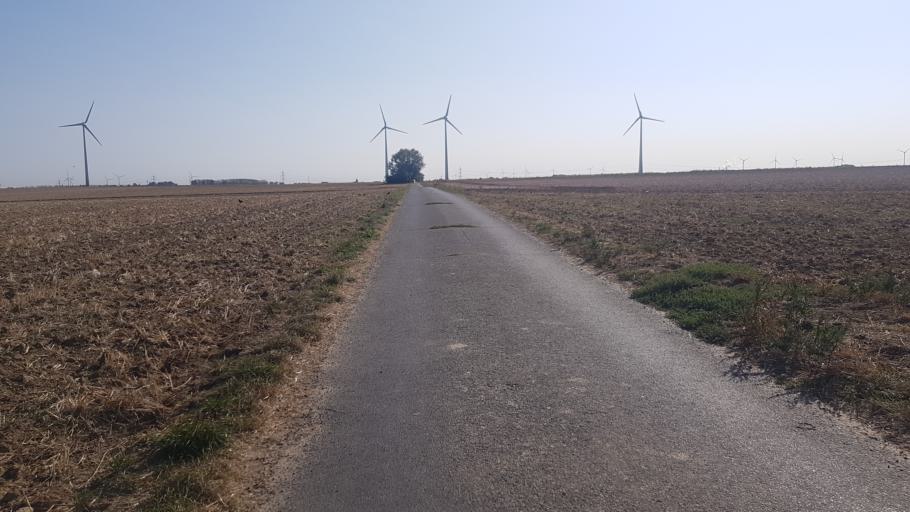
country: DE
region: North Rhine-Westphalia
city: Baesweiler
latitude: 50.9022
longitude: 6.1909
